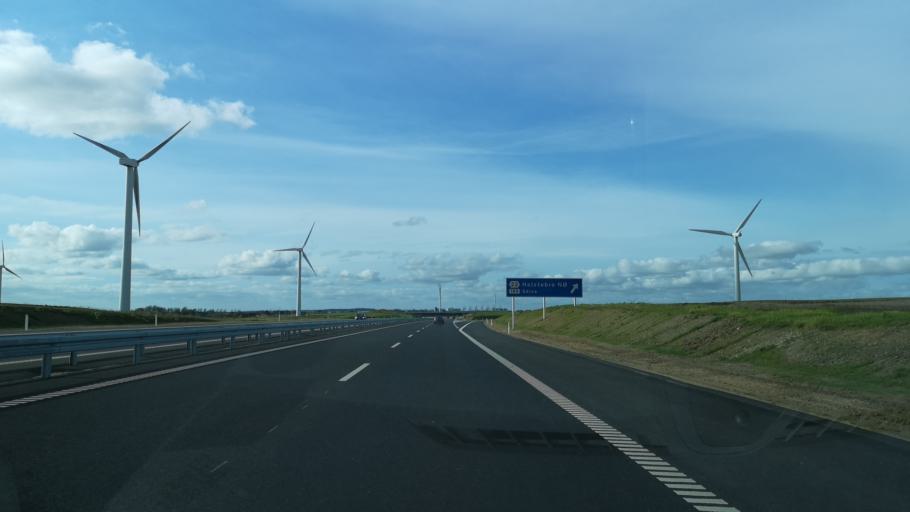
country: DK
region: Central Jutland
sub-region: Holstebro Kommune
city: Holstebro
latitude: 56.3834
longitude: 8.6640
